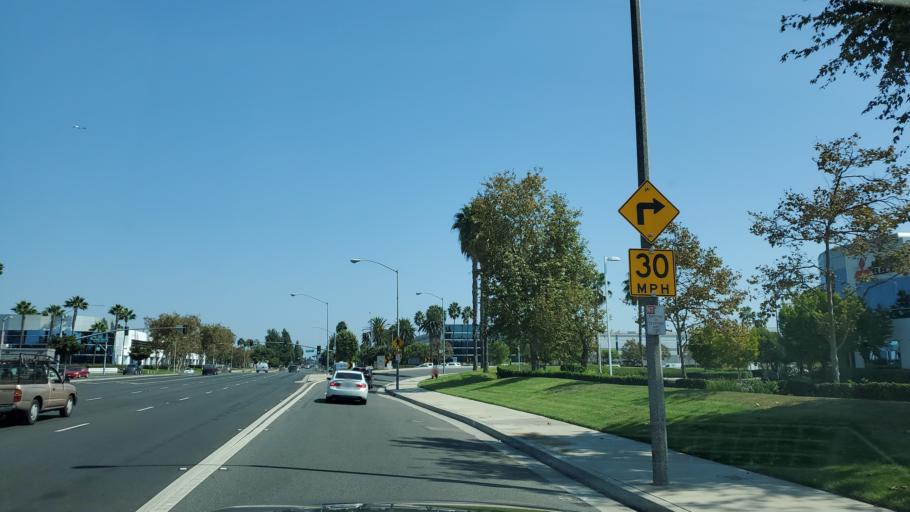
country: US
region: California
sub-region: Orange County
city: Cypress
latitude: 33.8028
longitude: -118.0297
